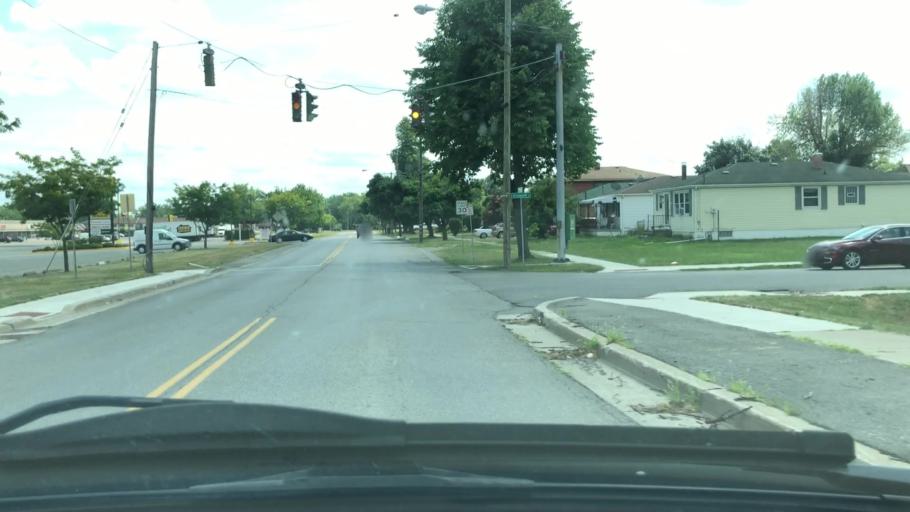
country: US
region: New York
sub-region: Erie County
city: Sloan
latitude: 42.8748
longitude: -78.7949
